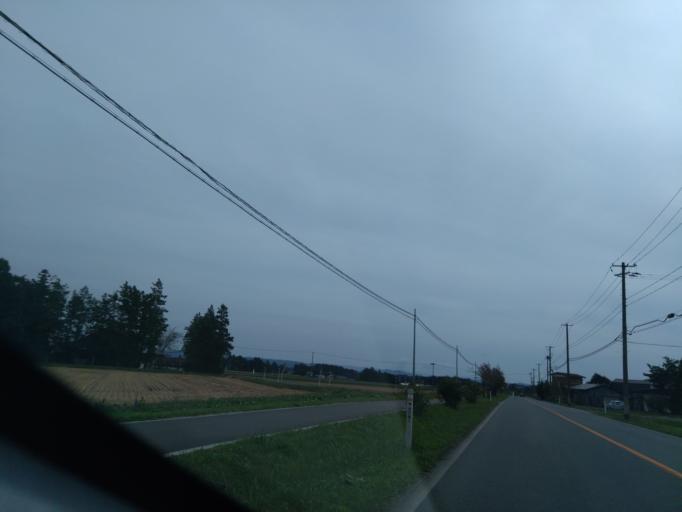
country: JP
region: Iwate
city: Hanamaki
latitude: 39.4335
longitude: 141.0827
